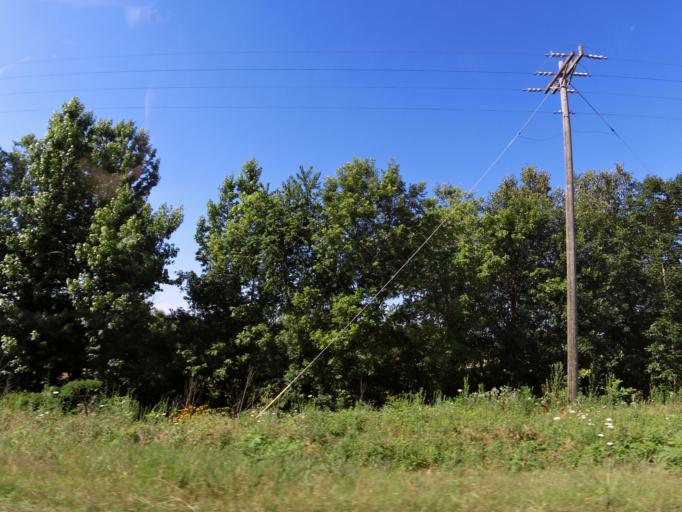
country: US
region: Arkansas
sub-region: Clay County
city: Piggott
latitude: 36.4305
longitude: -90.2930
